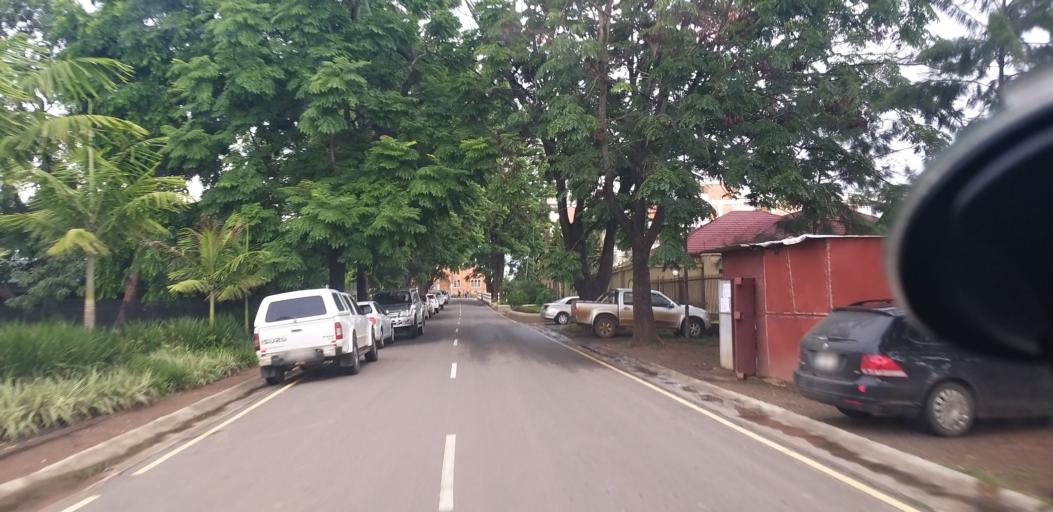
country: ZM
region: Lusaka
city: Lusaka
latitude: -15.4146
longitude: 28.2981
